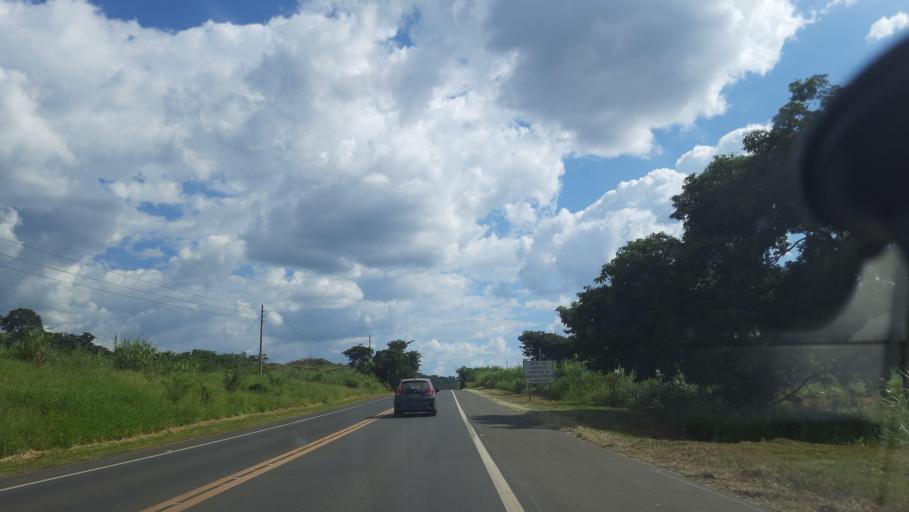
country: BR
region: Sao Paulo
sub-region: Sao Jose Do Rio Pardo
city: Sao Jose do Rio Pardo
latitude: -21.6393
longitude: -46.9055
